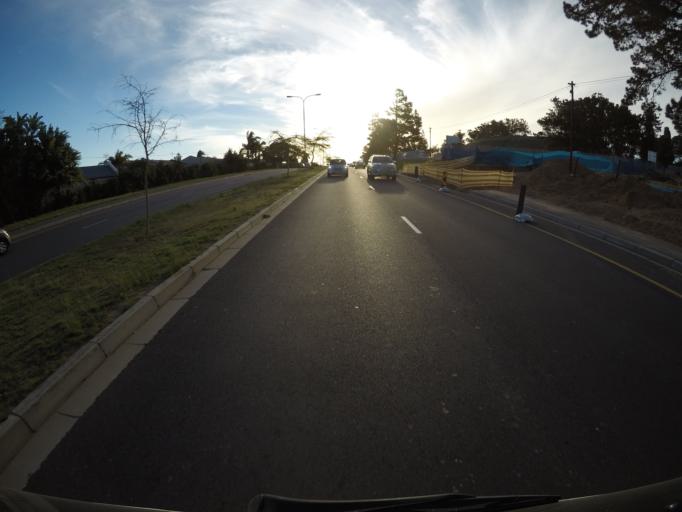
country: ZA
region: Western Cape
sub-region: City of Cape Town
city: Kraaifontein
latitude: -33.8584
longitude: 18.6797
